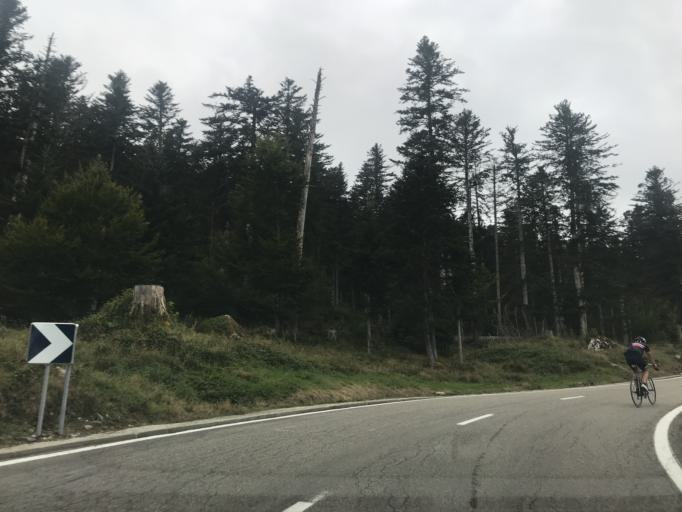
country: ES
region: Catalonia
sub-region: Provincia de Lleida
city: Les
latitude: 42.7666
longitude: 0.6603
